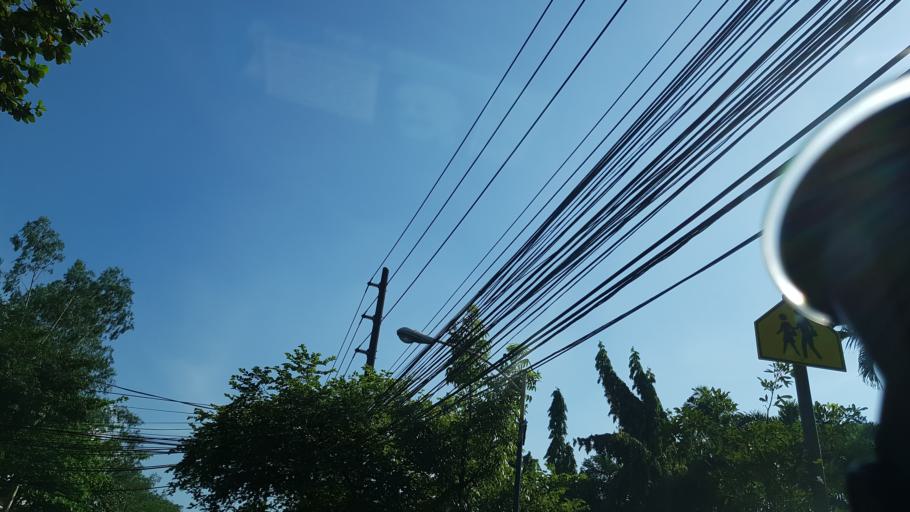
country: PH
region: Metro Manila
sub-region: Pasig
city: Pasig City
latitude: 14.5872
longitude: 121.0711
